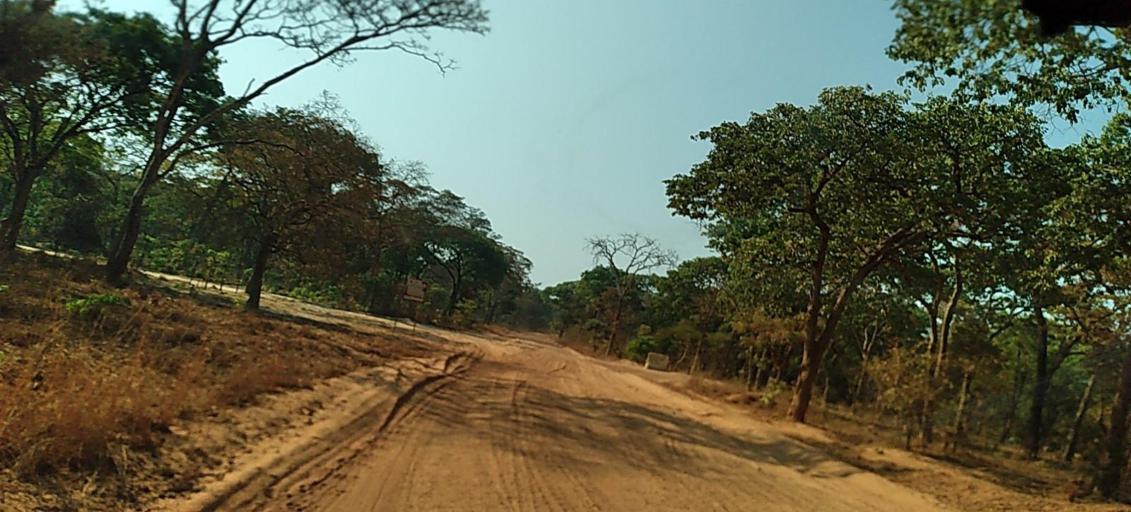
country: ZM
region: North-Western
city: Kasempa
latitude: -13.6835
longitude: 26.0259
